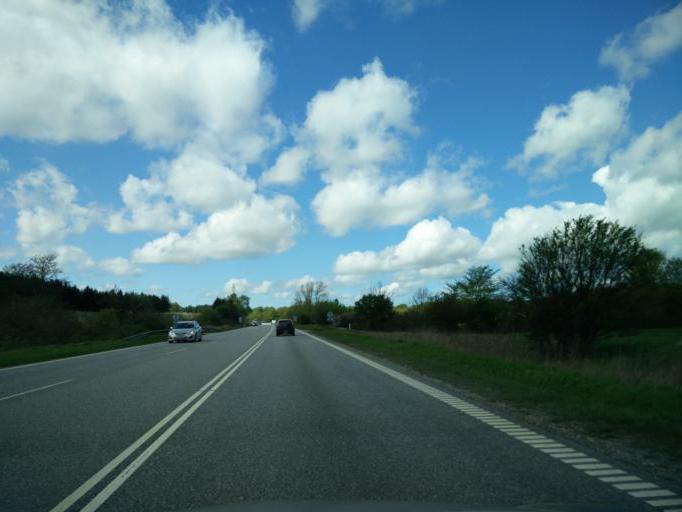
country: DK
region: Capital Region
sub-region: Allerod Kommune
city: Lillerod
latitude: 55.8779
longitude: 12.3068
